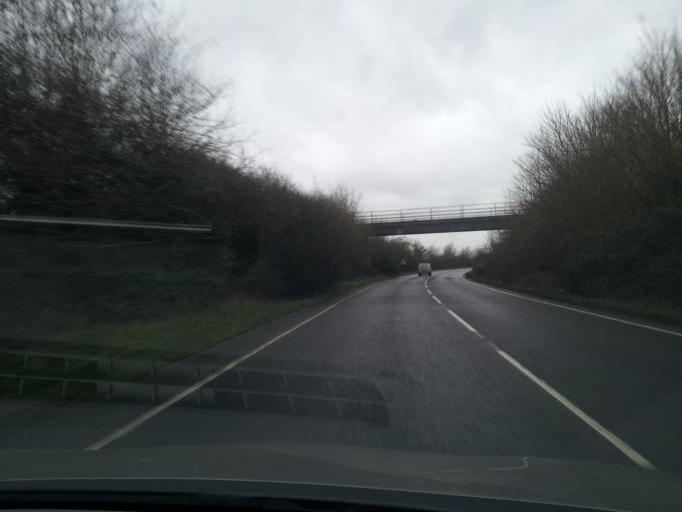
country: GB
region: England
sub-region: Norfolk
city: Diss
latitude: 52.3530
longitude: 1.0898
